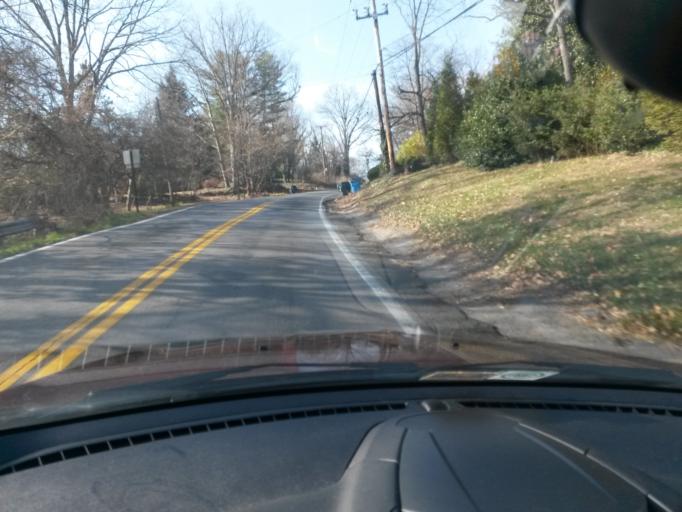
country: US
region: Virginia
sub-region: Roanoke County
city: Cave Spring
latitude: 37.2405
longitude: -79.9826
